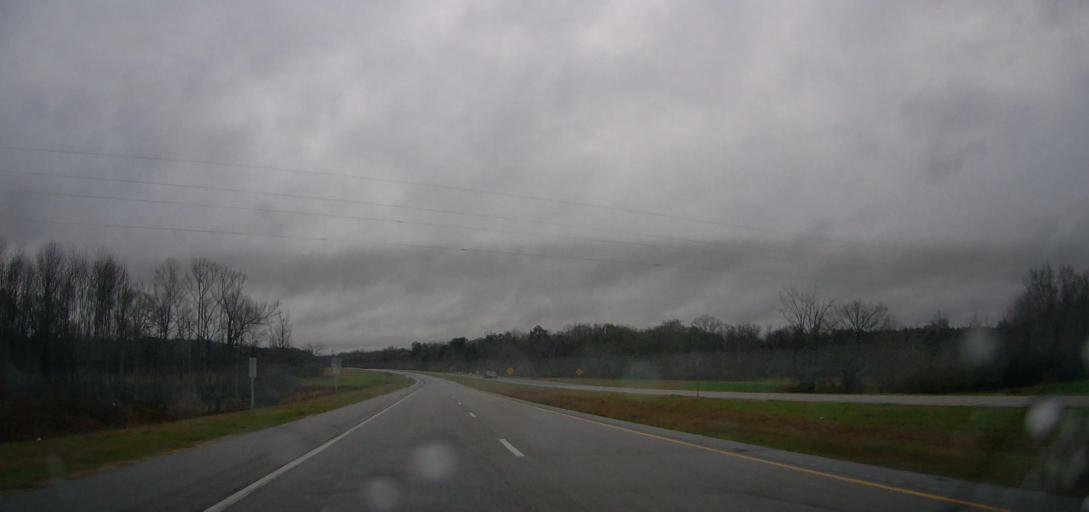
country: US
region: Alabama
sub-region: Bibb County
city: Centreville
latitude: 32.9363
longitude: -87.0636
